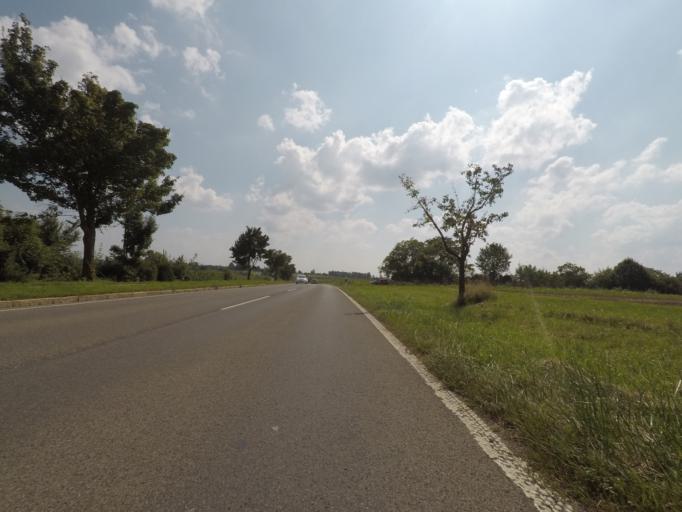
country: DE
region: Baden-Wuerttemberg
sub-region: Regierungsbezirk Stuttgart
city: Weinstadt-Endersbach
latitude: 48.7746
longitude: 9.3893
